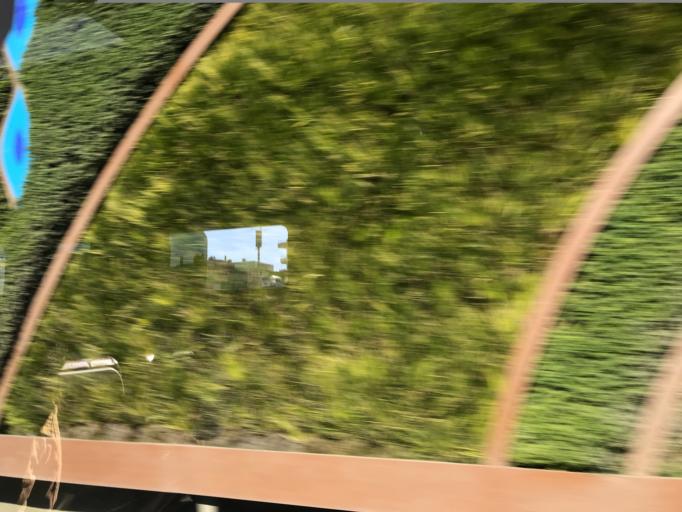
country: TR
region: Istanbul
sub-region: Atasehir
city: Atasehir
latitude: 40.9545
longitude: 29.1166
